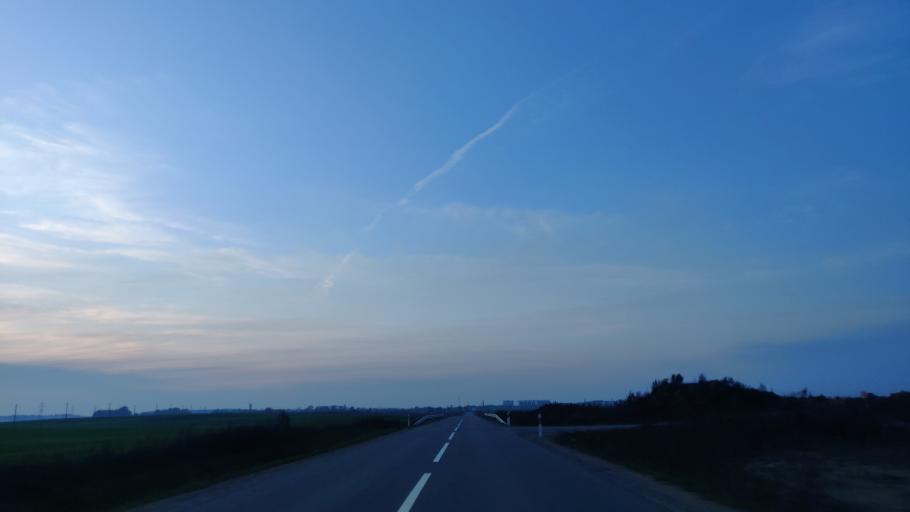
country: LT
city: Lentvaris
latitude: 54.6023
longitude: 25.0068
